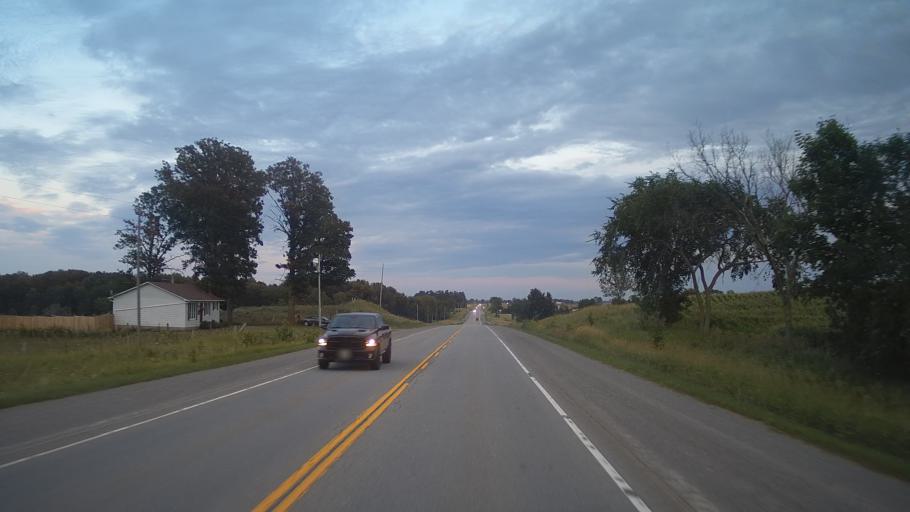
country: CA
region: Ontario
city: Pembroke
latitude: 45.6957
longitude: -76.9598
